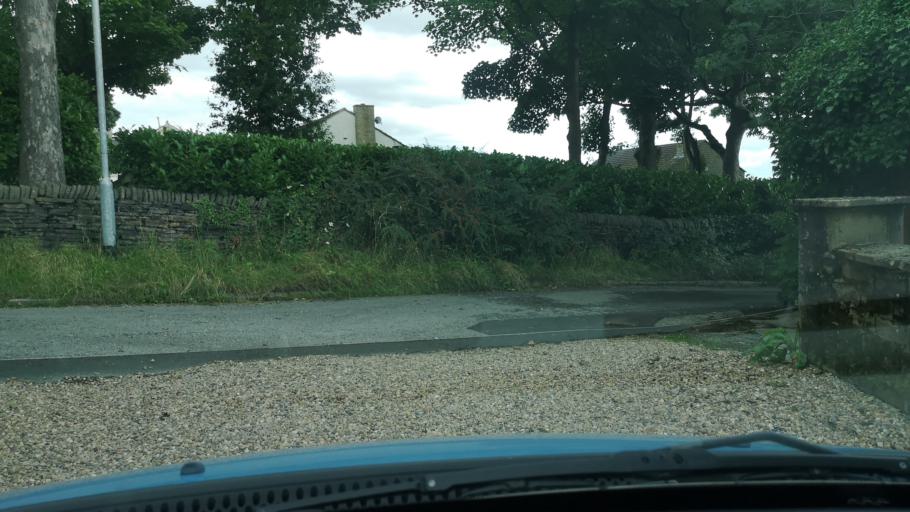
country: GB
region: England
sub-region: Kirklees
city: Clayton West
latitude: 53.6305
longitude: -1.6416
